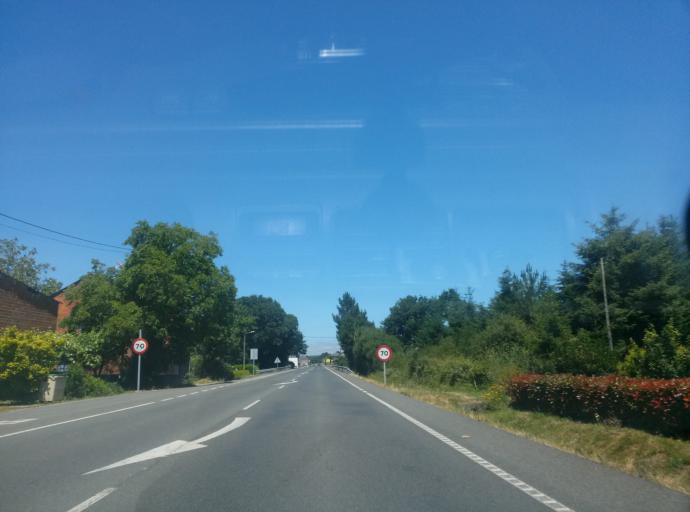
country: ES
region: Galicia
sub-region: Provincia de Lugo
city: Mos
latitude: 43.1762
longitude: -7.4784
